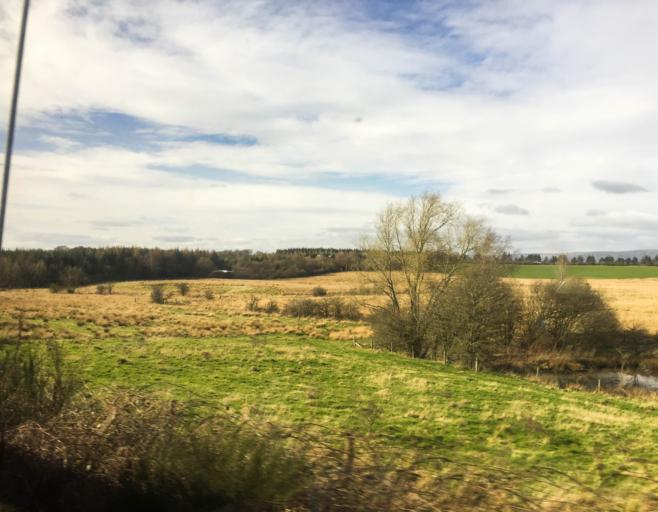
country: GB
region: Scotland
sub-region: North Lanarkshire
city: Stepps
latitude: 55.8894
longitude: -4.1575
